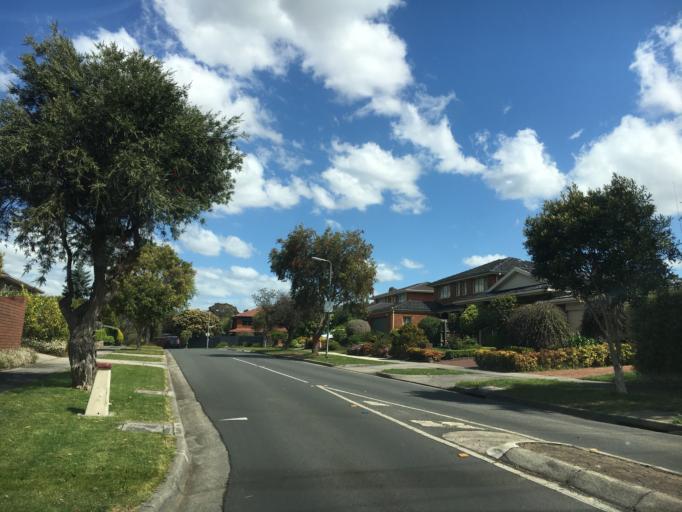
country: AU
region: Victoria
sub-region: Whitehorse
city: Vermont South
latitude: -37.8838
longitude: 145.1819
